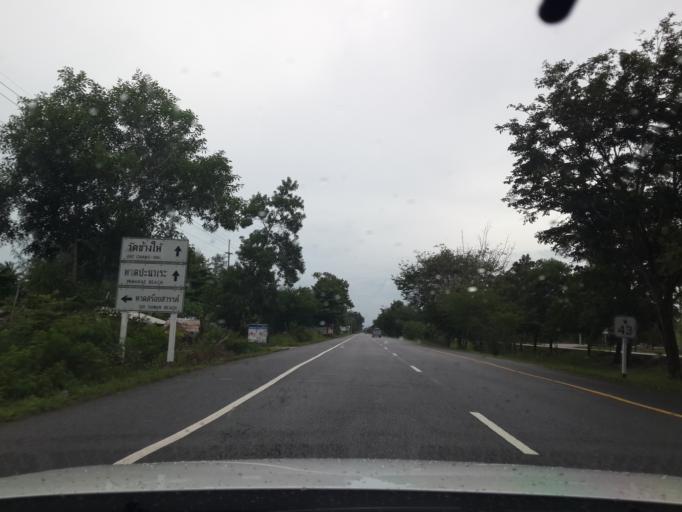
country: TH
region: Songkhla
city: Thepha
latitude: 6.8895
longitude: 100.9332
